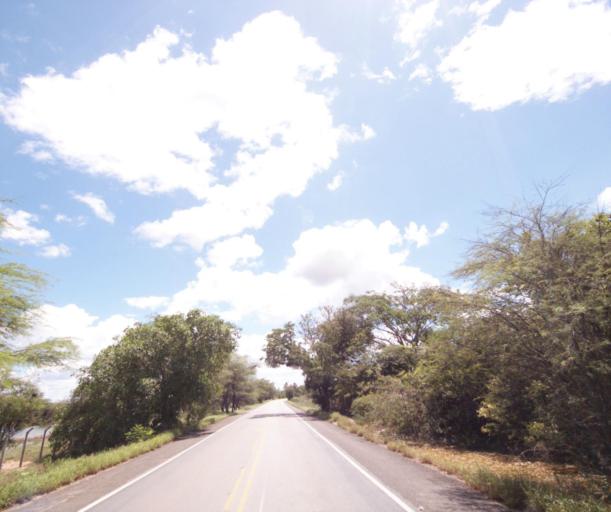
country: BR
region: Bahia
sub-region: Brumado
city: Brumado
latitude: -14.2437
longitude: -41.7269
